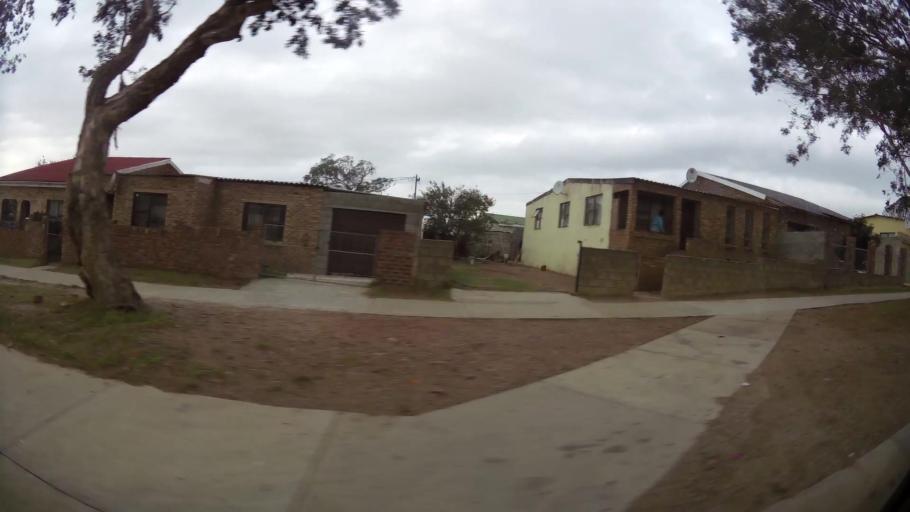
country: ZA
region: Eastern Cape
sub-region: Nelson Mandela Bay Metropolitan Municipality
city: Port Elizabeth
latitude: -33.9118
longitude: 25.5453
